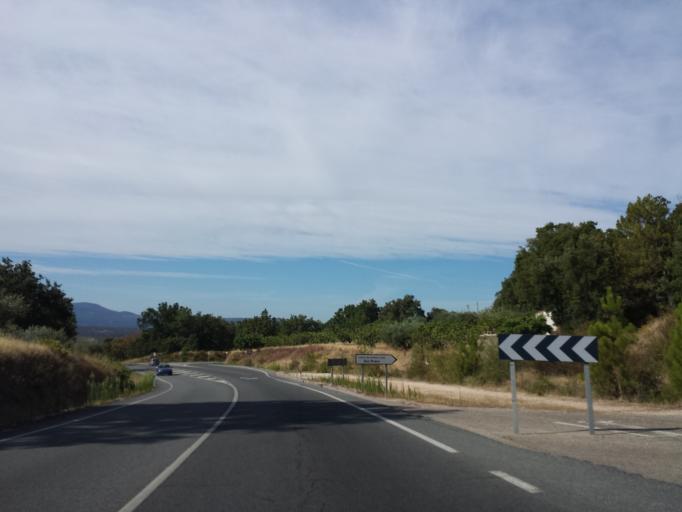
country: ES
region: Castille and Leon
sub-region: Provincia de Avila
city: Piedralaves
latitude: 40.3028
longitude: -4.7192
